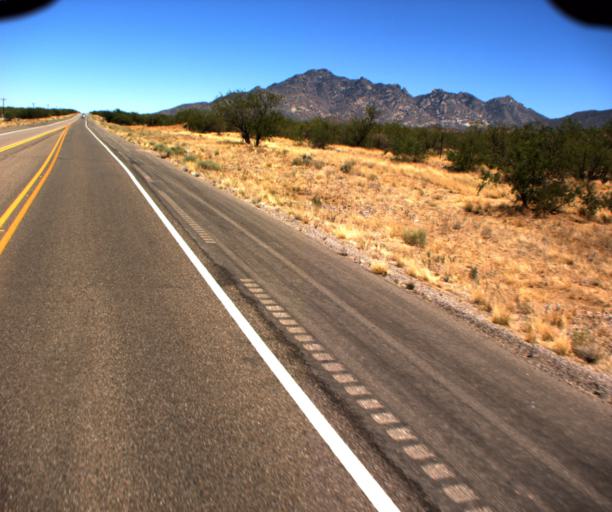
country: US
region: Arizona
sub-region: Pima County
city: Sells
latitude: 32.0158
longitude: -111.6334
